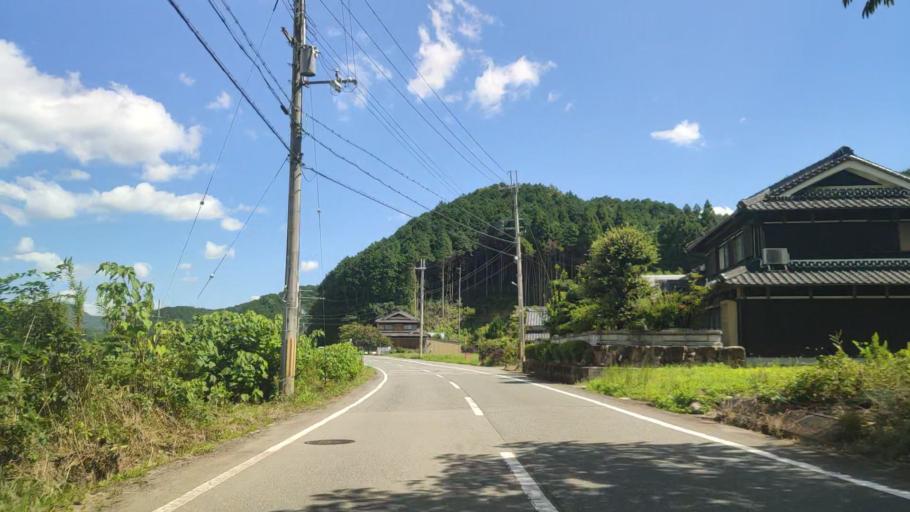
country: JP
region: Hyogo
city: Nishiwaki
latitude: 35.1353
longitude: 135.0265
